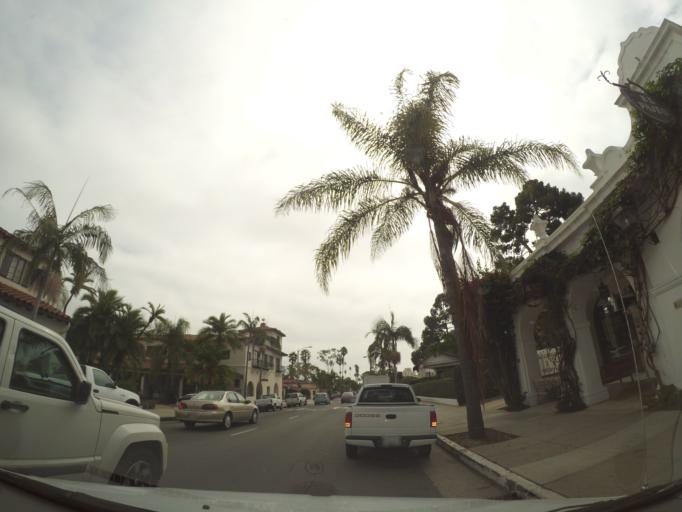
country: US
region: California
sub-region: Santa Barbara County
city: Santa Barbara
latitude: 34.4211
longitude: -119.6989
